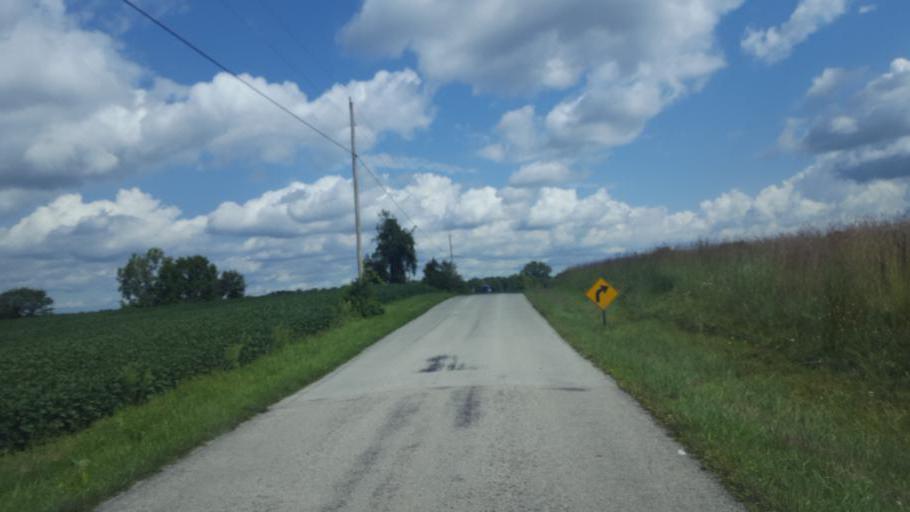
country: US
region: Ohio
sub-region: Huron County
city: Monroeville
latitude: 41.1672
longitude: -82.6656
